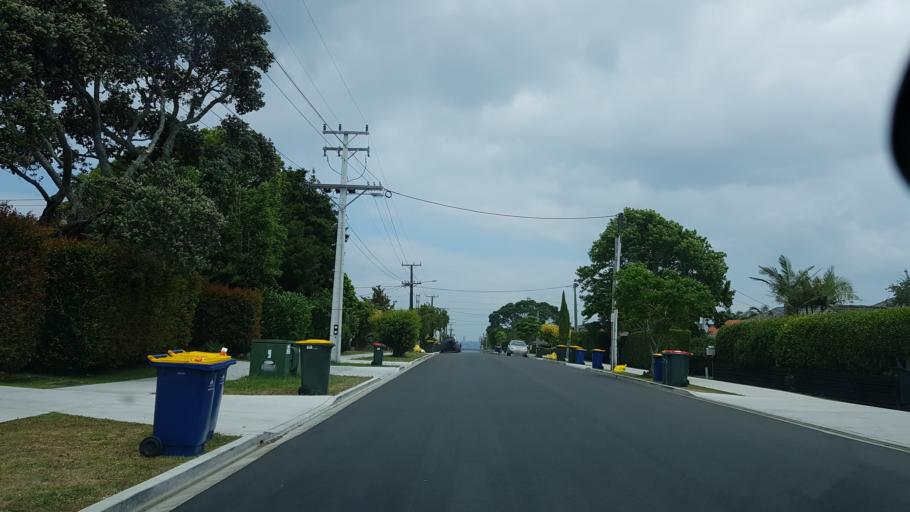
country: NZ
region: Auckland
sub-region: Auckland
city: North Shore
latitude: -36.8000
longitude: 174.7769
